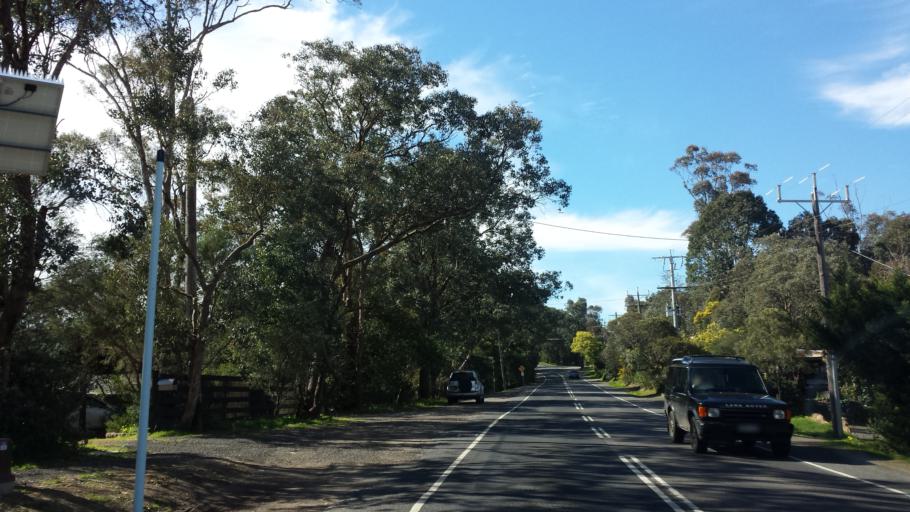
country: AU
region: Victoria
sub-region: Nillumbik
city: North Warrandyte
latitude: -37.7304
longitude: 145.2286
